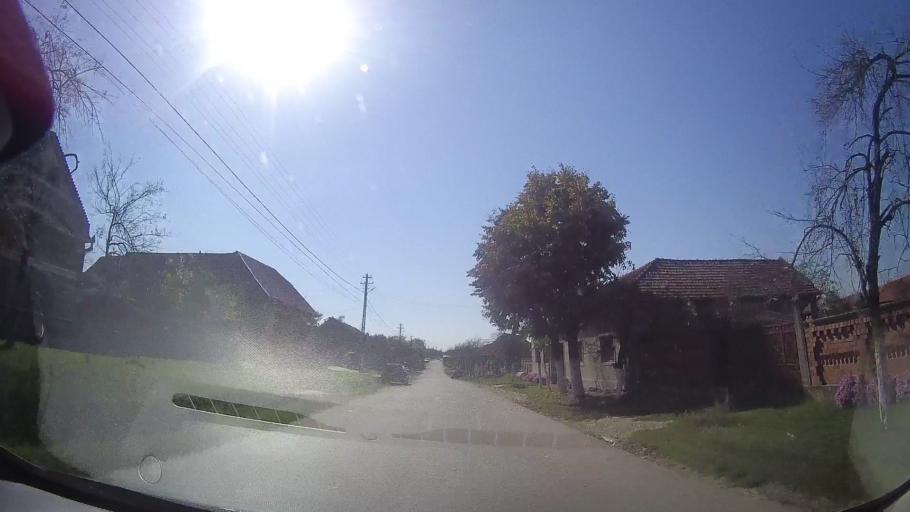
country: RO
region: Timis
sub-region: Comuna Bethausen
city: Bethausen
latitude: 45.8630
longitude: 21.9703
